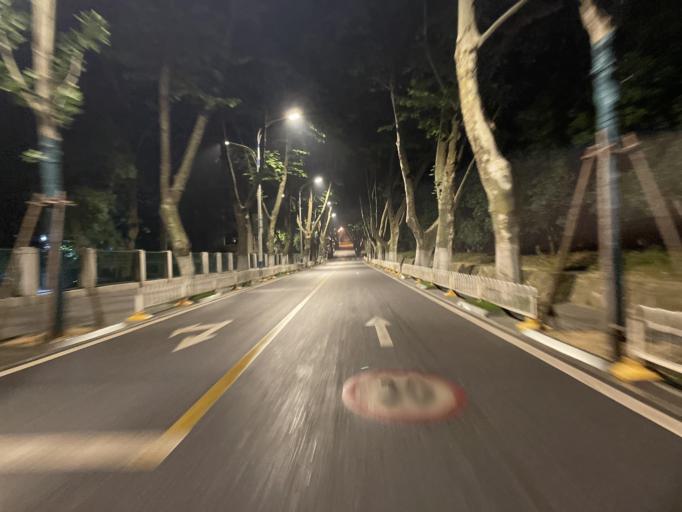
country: CN
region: Hubei
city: Guanshan
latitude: 30.5175
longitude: 114.4073
